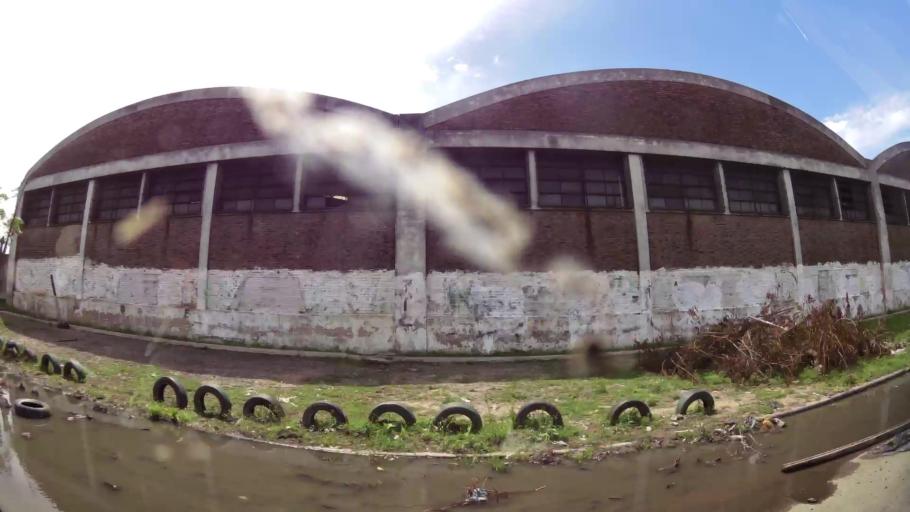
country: AR
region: Buenos Aires
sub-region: Partido de Quilmes
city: Quilmes
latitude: -34.7579
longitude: -58.3012
